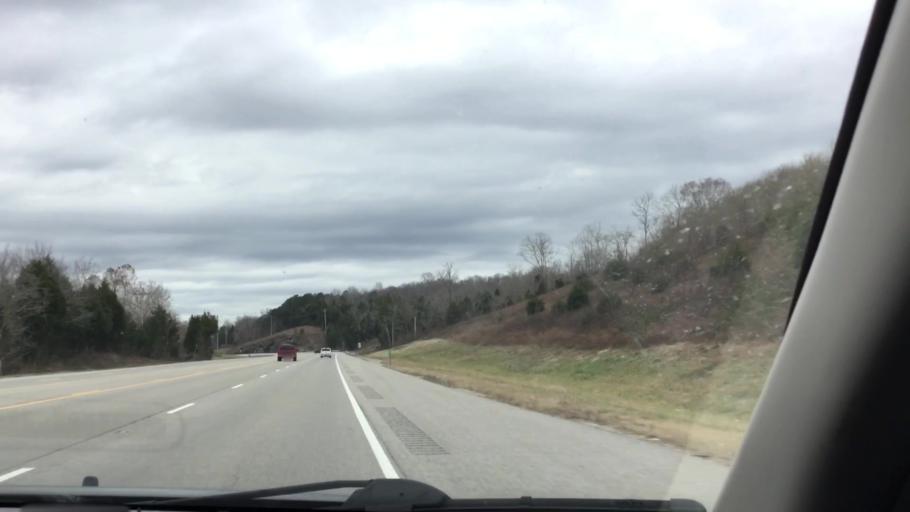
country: US
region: Tennessee
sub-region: Lewis County
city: Hohenwald
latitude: 35.5813
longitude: -87.4405
